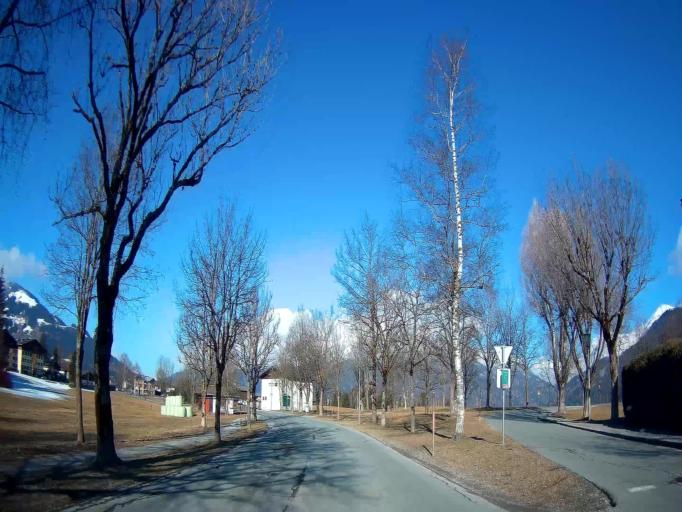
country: AT
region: Salzburg
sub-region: Politischer Bezirk Zell am See
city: Saalfelden am Steinernen Meer
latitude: 47.4335
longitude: 12.8497
